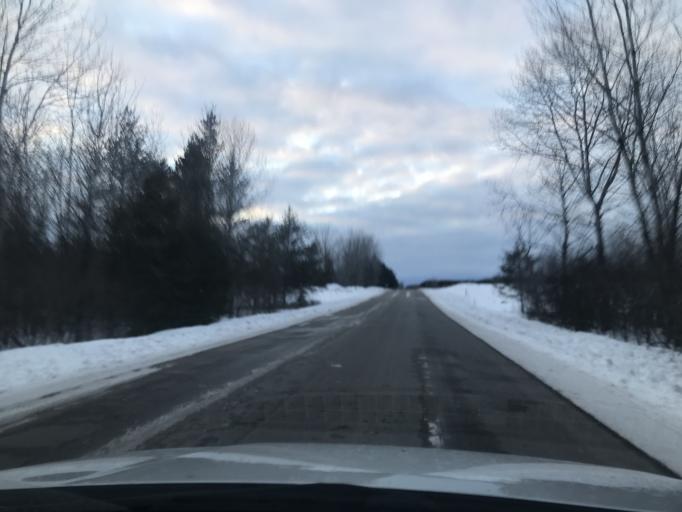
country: US
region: Wisconsin
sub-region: Marinette County
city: Peshtigo
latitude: 45.1647
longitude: -87.7505
